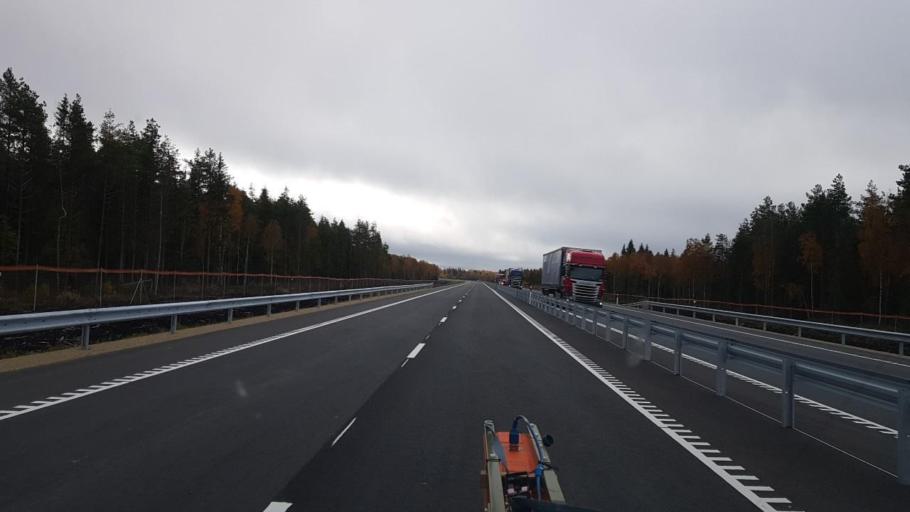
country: EE
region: Jaervamaa
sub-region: Paide linn
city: Paide
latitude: 59.0186
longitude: 25.5501
